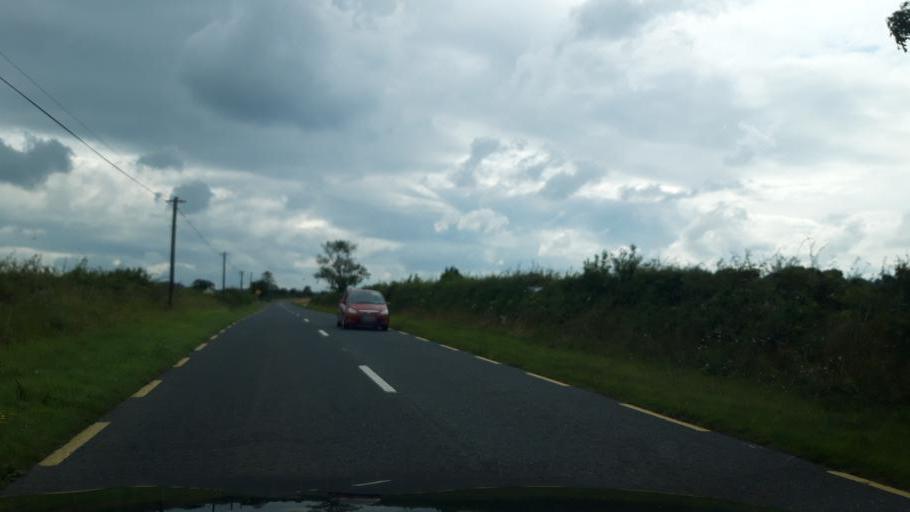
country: IE
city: Ballylinan
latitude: 52.9193
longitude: -7.0660
